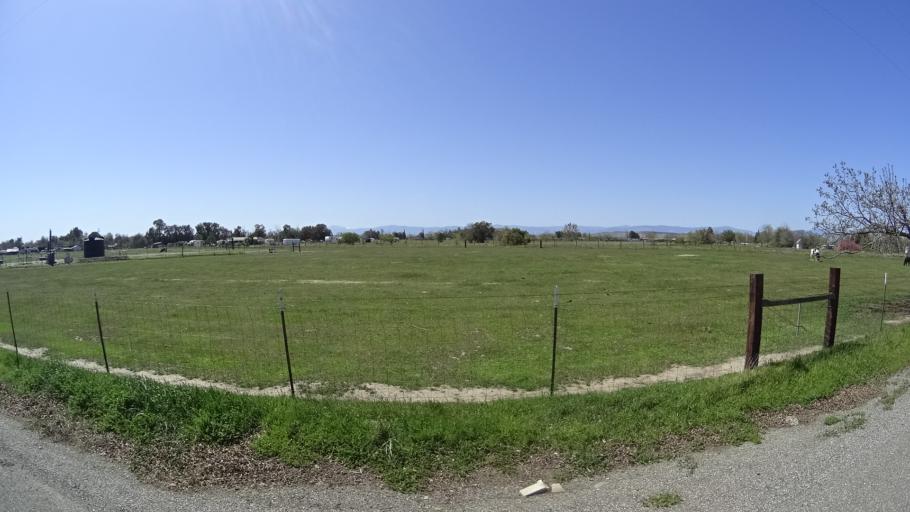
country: US
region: California
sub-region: Glenn County
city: Orland
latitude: 39.7835
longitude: -122.2394
